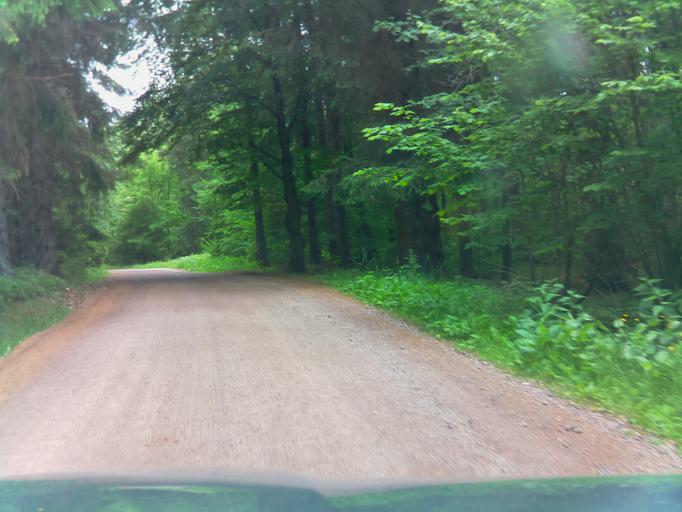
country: DE
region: Thuringia
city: Suhl
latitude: 50.6274
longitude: 10.6774
